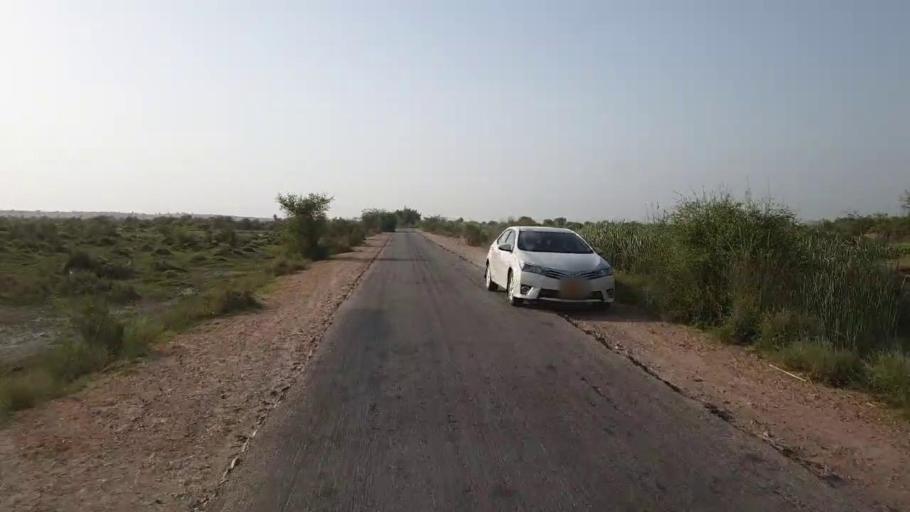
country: PK
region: Sindh
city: Jam Sahib
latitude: 26.4573
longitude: 68.8598
